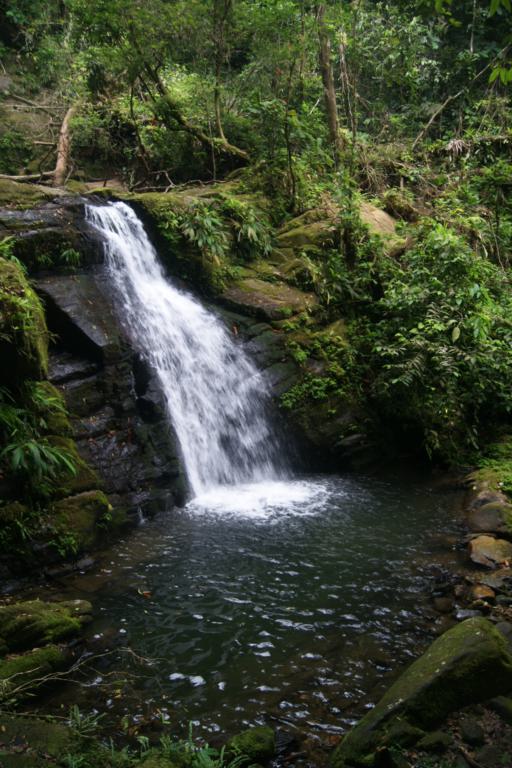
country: BR
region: Sao Paulo
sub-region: Mongagua
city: Mongagua
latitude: -24.0336
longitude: -46.7052
